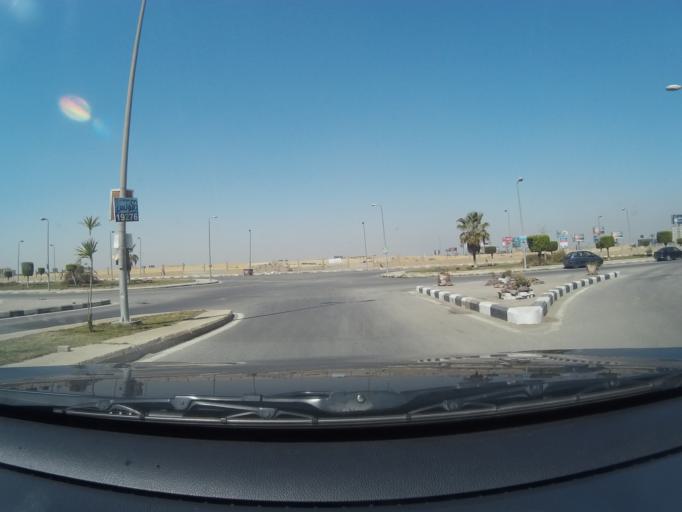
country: EG
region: Muhafazat al Qahirah
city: Cairo
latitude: 30.0152
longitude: 31.4112
